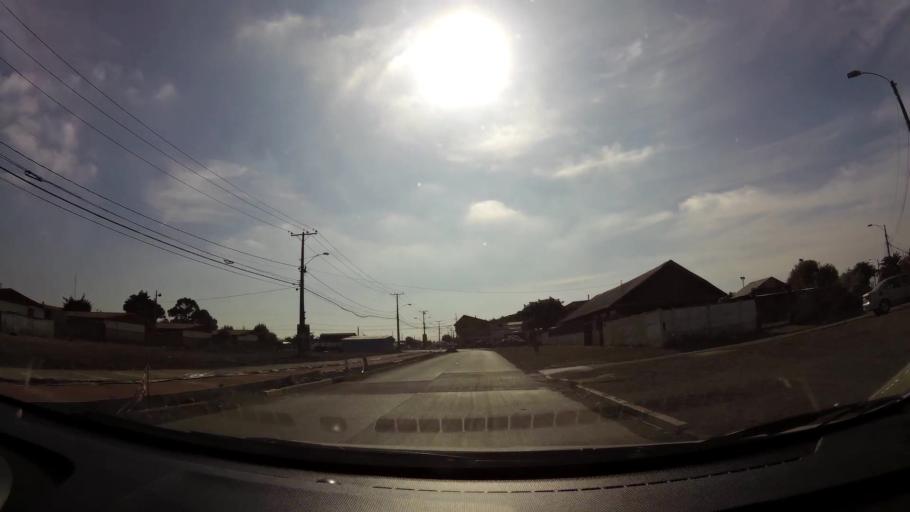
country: CL
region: Biobio
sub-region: Provincia de Concepcion
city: Talcahuano
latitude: -36.7865
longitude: -73.1165
